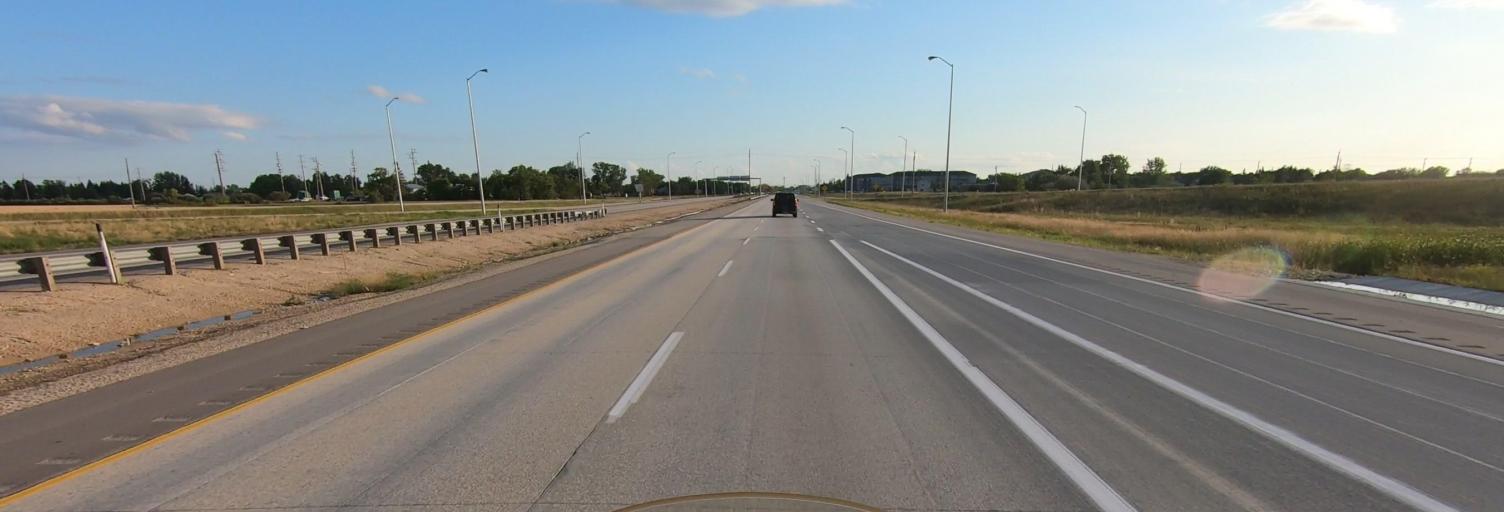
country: CA
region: Manitoba
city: Winnipeg
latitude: 49.9482
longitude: -97.0311
